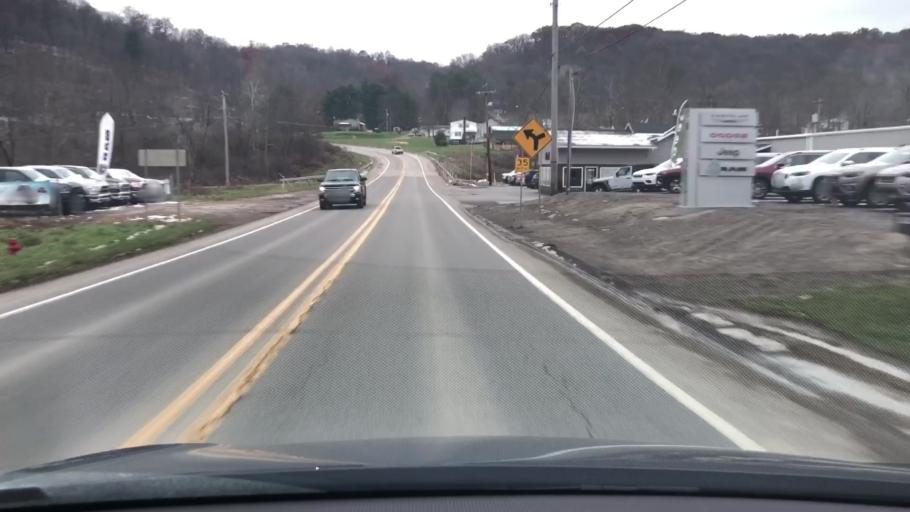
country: US
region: Pennsylvania
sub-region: Clarion County
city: Clarion
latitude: 41.0149
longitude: -79.2977
